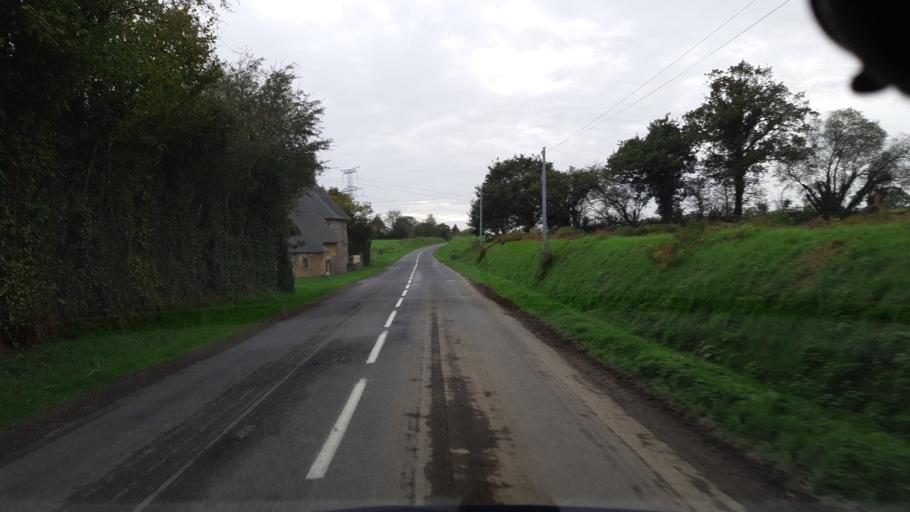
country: FR
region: Lower Normandy
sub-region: Departement de la Manche
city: Hambye
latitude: 48.9852
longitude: -1.2126
